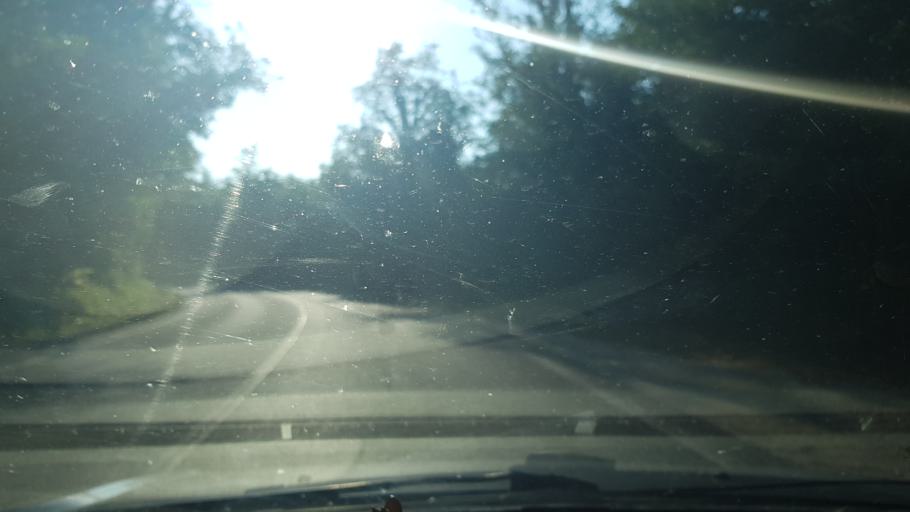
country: IT
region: Friuli Venezia Giulia
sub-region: Provincia di Gorizia
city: Farra d'Isonzo
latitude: 45.8930
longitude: 13.5318
